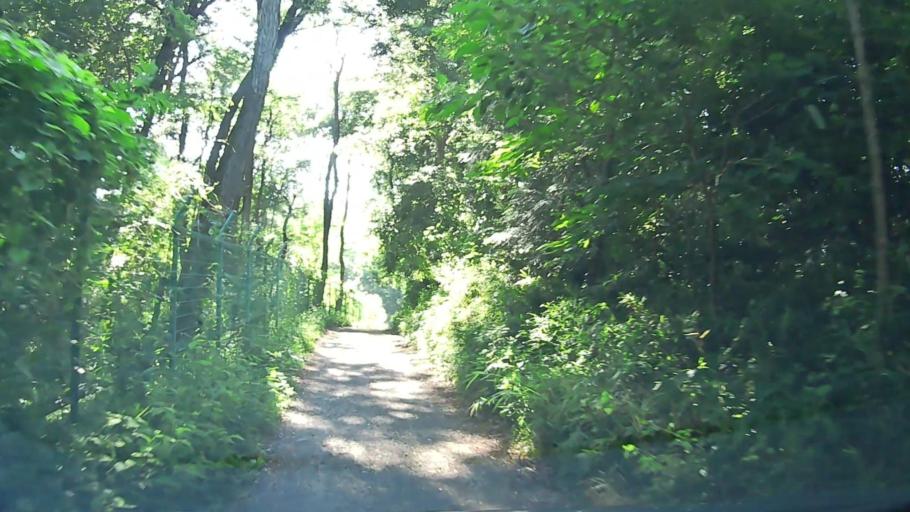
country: JP
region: Saitama
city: Sayama
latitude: 35.7835
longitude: 139.3917
